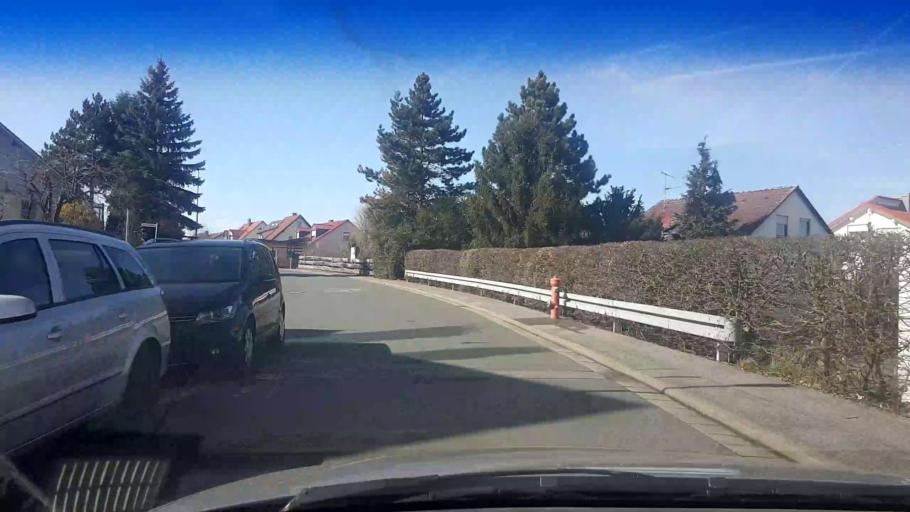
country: DE
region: Bavaria
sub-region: Upper Franconia
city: Bischberg
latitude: 49.9130
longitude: 10.8222
